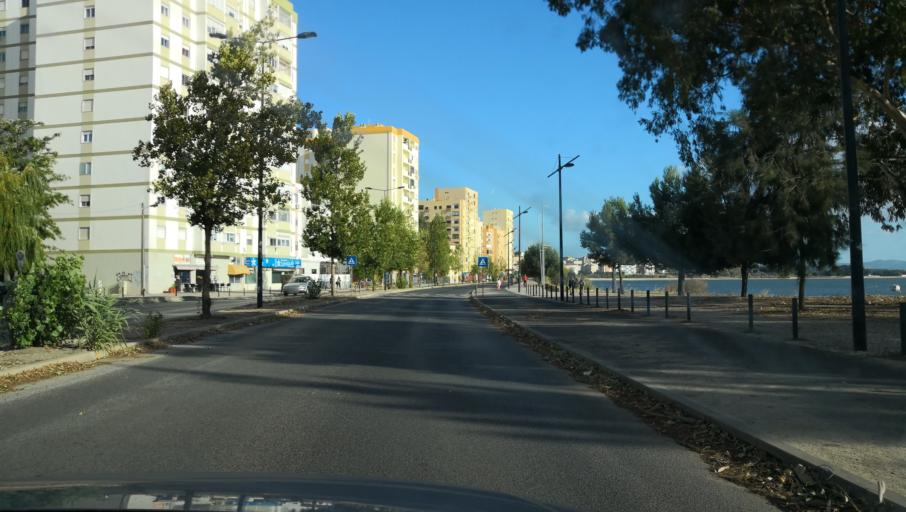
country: PT
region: Setubal
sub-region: Barreiro
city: Barreiro
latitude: 38.6532
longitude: -9.0740
